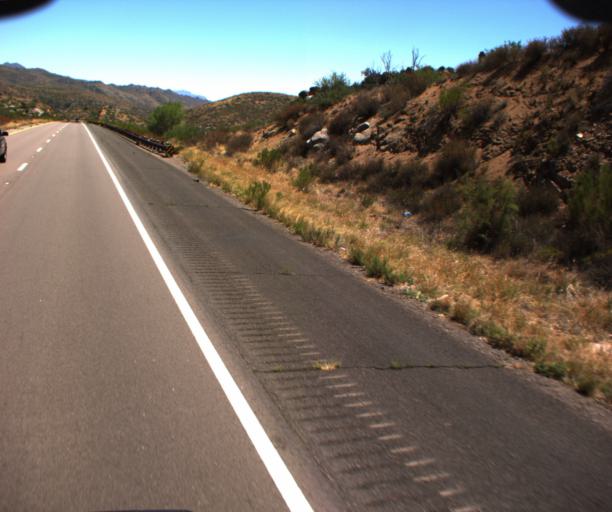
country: US
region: Arizona
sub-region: Gila County
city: Tonto Basin
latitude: 33.8472
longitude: -111.4701
